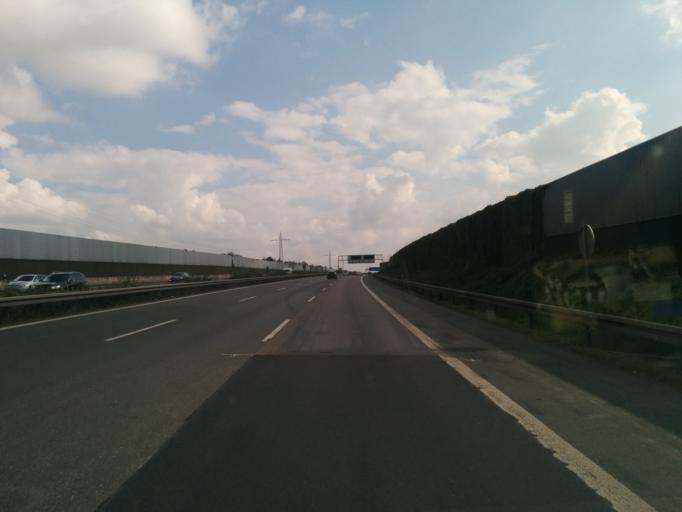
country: DE
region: North Rhine-Westphalia
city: Castrop-Rauxel
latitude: 51.5983
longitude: 7.3357
